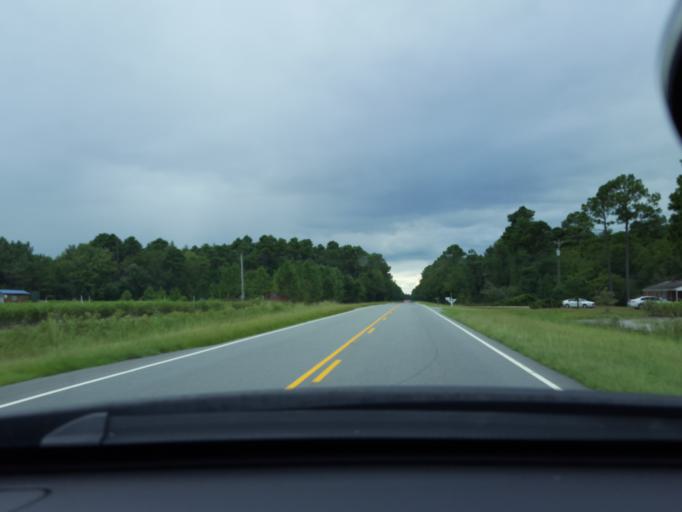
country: US
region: North Carolina
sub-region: Bladen County
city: Elizabethtown
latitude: 34.7330
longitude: -78.4345
